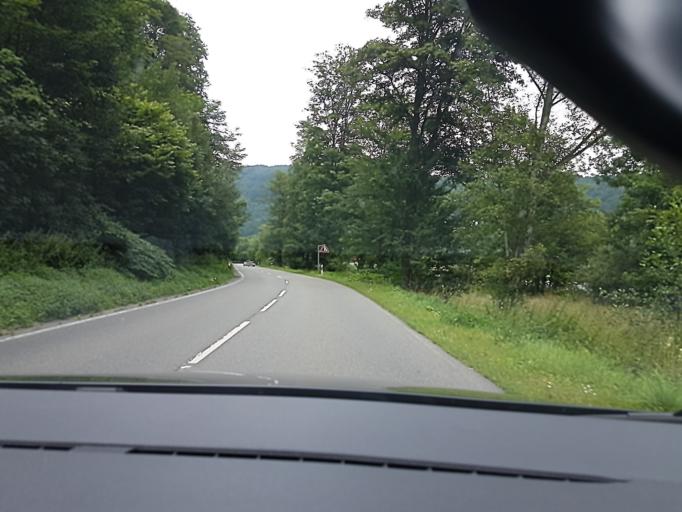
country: DE
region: Rheinland-Pfalz
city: Nassau
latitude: 50.3124
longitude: 7.7942
